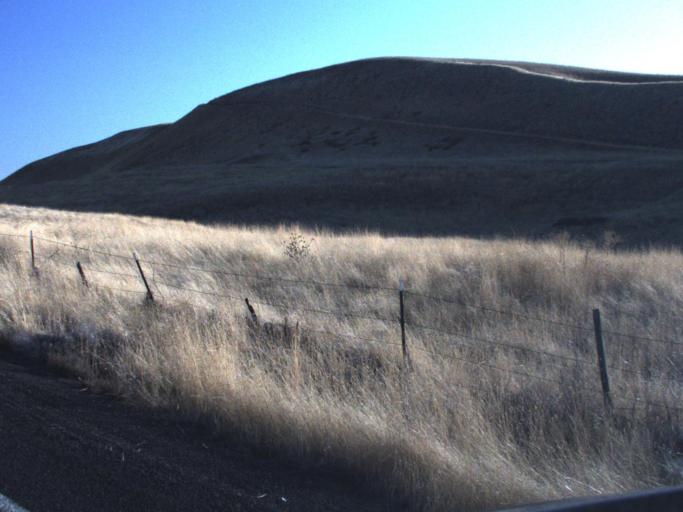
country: US
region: Washington
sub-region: Walla Walla County
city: Waitsburg
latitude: 46.6424
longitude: -118.2457
